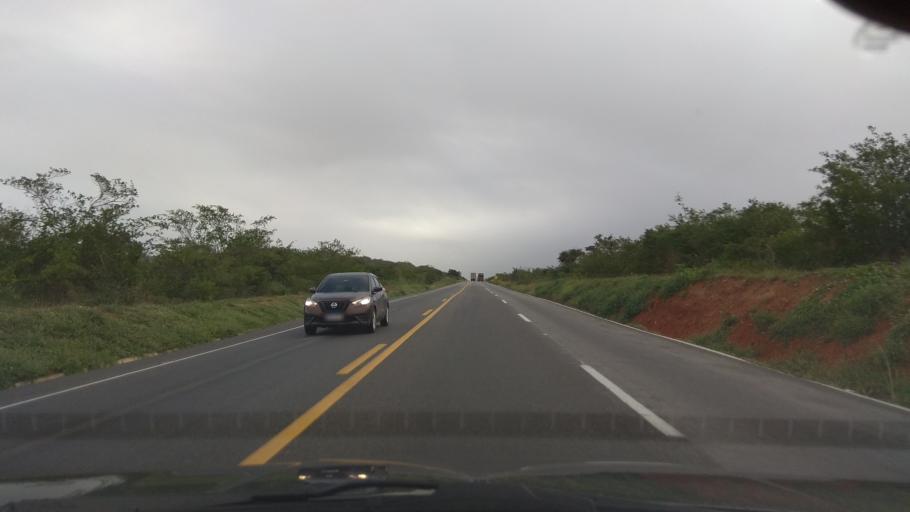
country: BR
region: Bahia
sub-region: Santa Ines
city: Santa Ines
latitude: -13.0327
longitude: -39.9645
